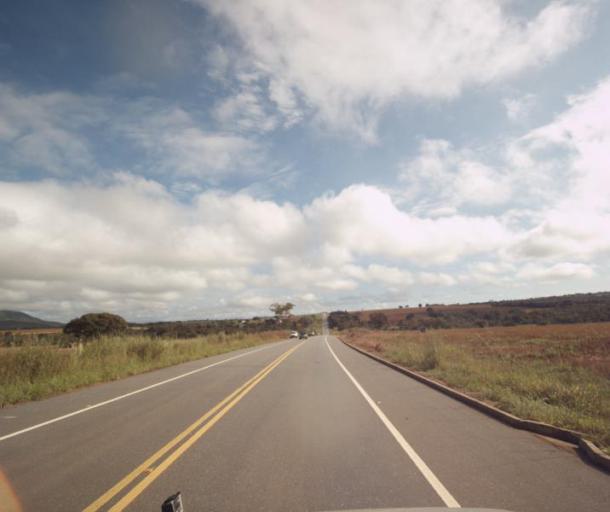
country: BR
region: Goias
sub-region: Barro Alto
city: Barro Alto
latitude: -15.2670
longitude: -48.6861
